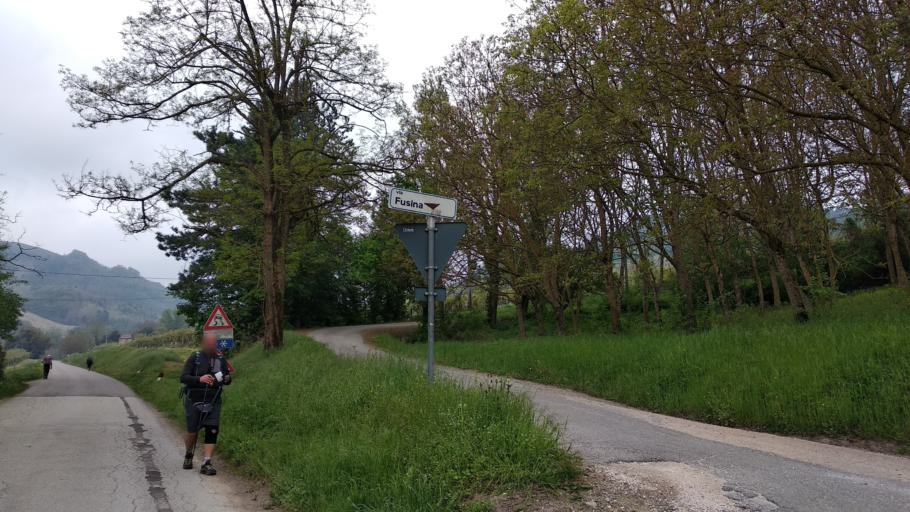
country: IT
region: Emilia-Romagna
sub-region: Forli-Cesena
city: Modigliana
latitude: 44.1444
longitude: 11.7999
